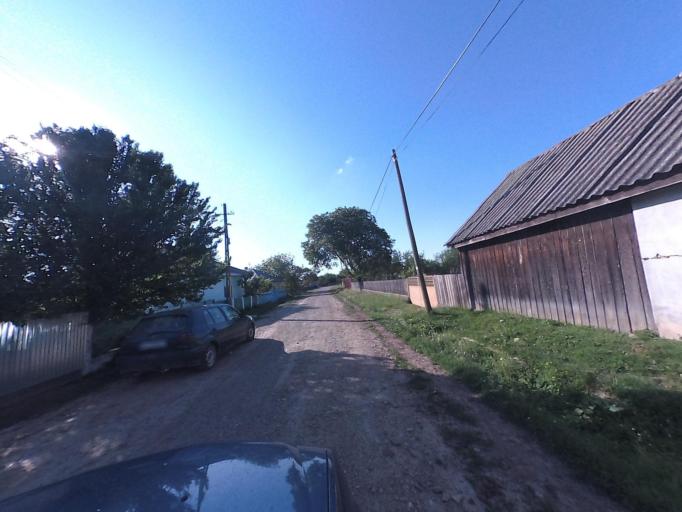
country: RO
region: Neamt
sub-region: Comuna Cordun
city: Pildesti
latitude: 46.9817
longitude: 26.8088
